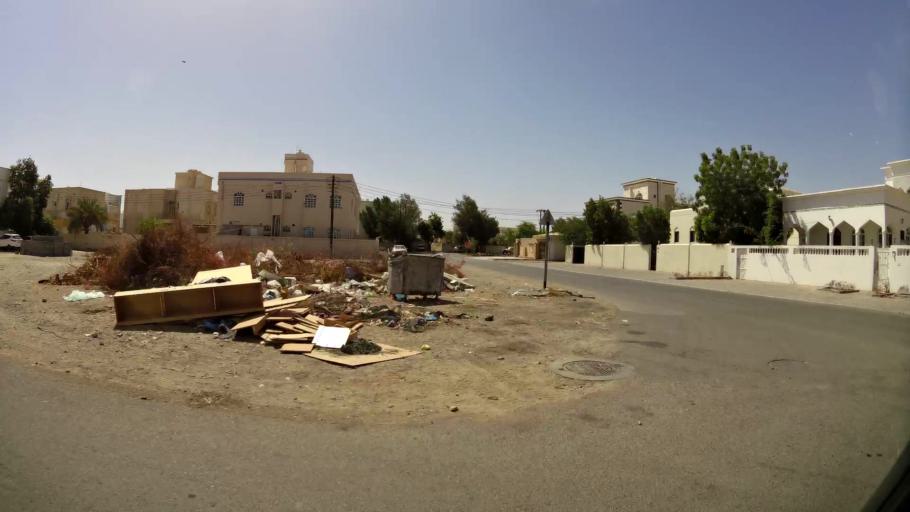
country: OM
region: Muhafazat Masqat
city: As Sib al Jadidah
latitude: 23.6045
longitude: 58.2422
